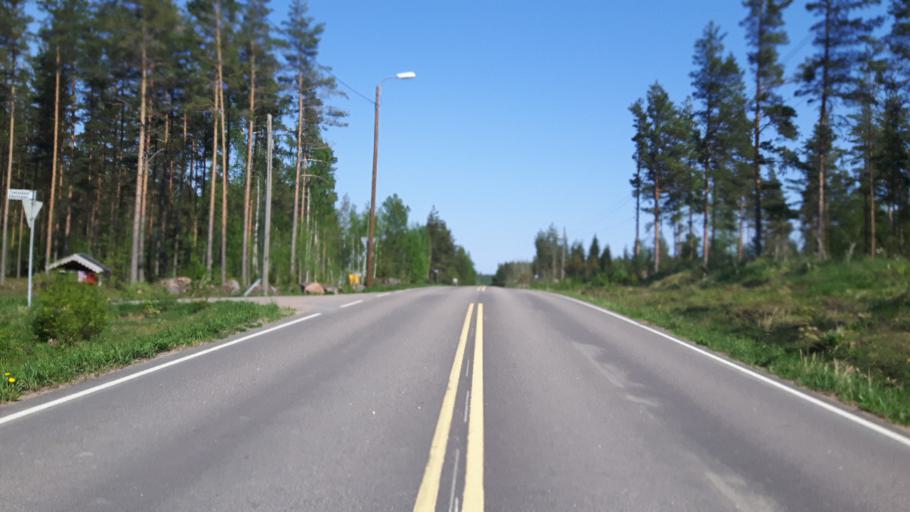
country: FI
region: Kymenlaakso
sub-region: Kotka-Hamina
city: Broby
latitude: 60.4916
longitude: 26.6936
